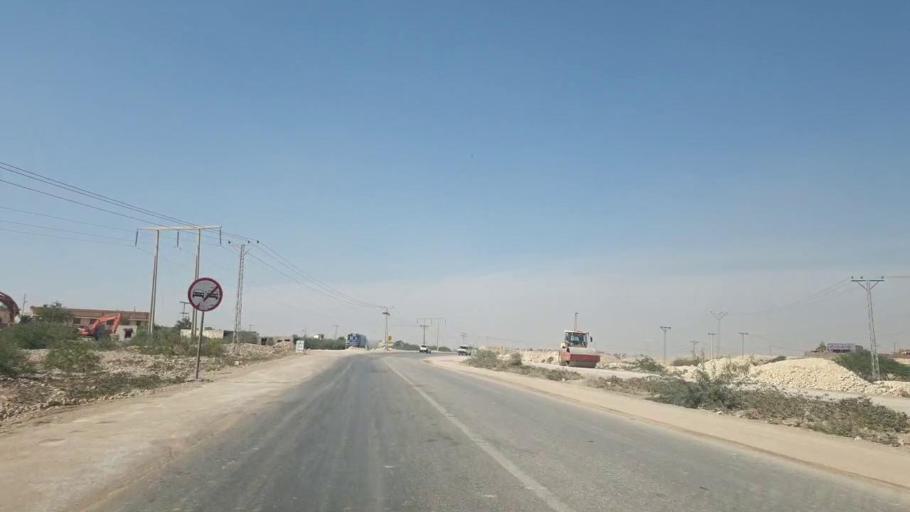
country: PK
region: Sindh
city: Hala
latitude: 25.7355
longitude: 68.2904
